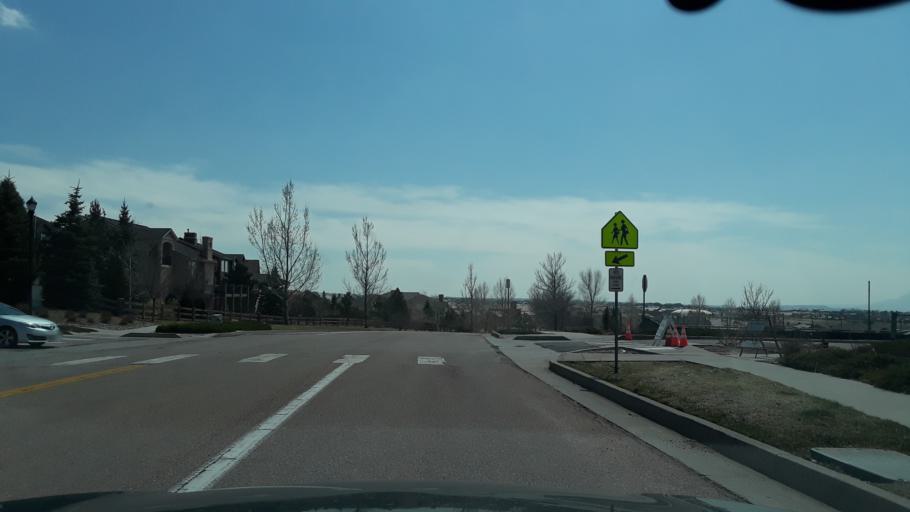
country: US
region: Colorado
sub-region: El Paso County
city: Gleneagle
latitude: 39.0323
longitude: -104.7907
